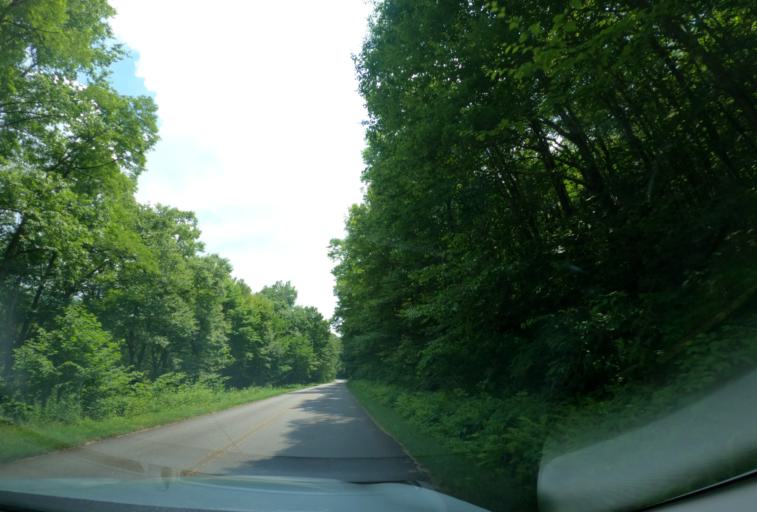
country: US
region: North Carolina
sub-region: Transylvania County
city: Brevard
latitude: 35.3472
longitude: -82.8110
